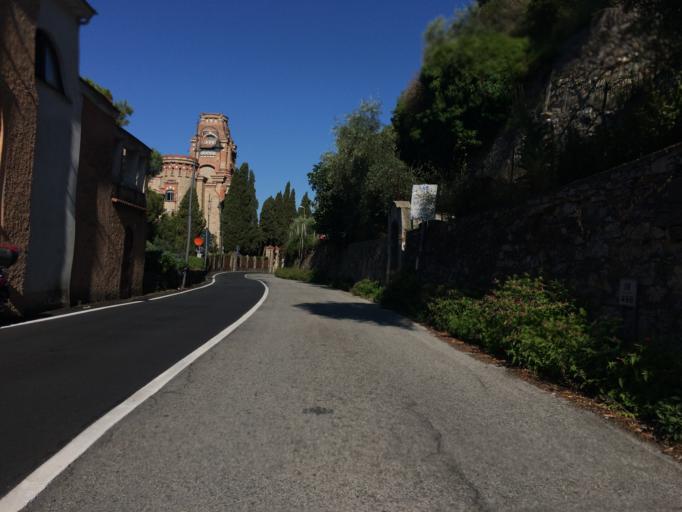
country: IT
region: Liguria
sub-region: Provincia di Genova
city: Zoagli
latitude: 44.3339
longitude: 9.2755
